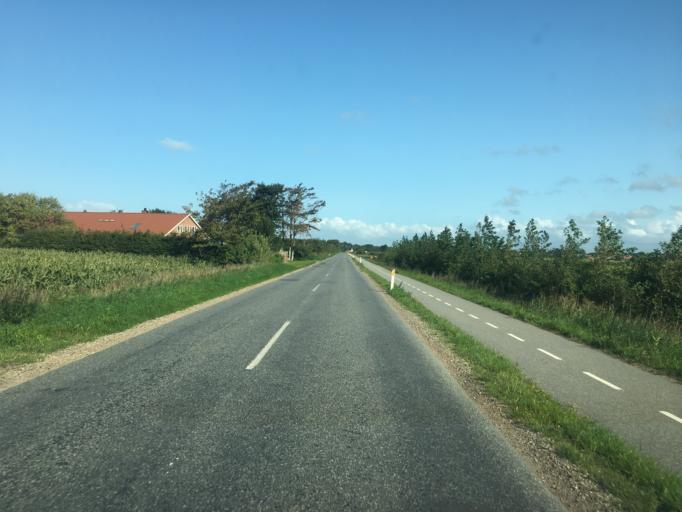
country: DK
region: South Denmark
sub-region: Tonder Kommune
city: Sherrebek
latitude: 55.1425
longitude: 8.7599
